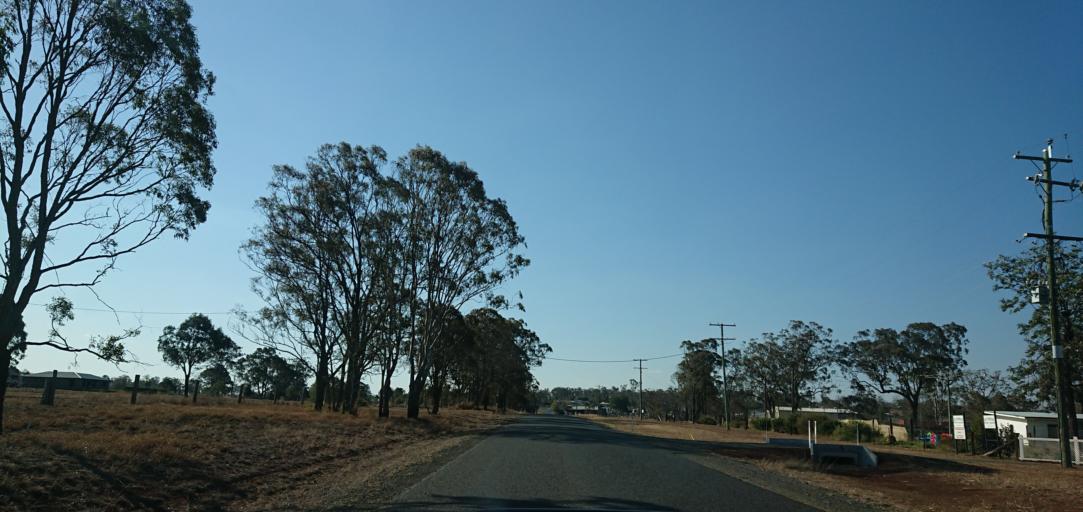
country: AU
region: Queensland
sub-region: Toowoomba
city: Westbrook
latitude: -27.6857
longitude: 151.7140
